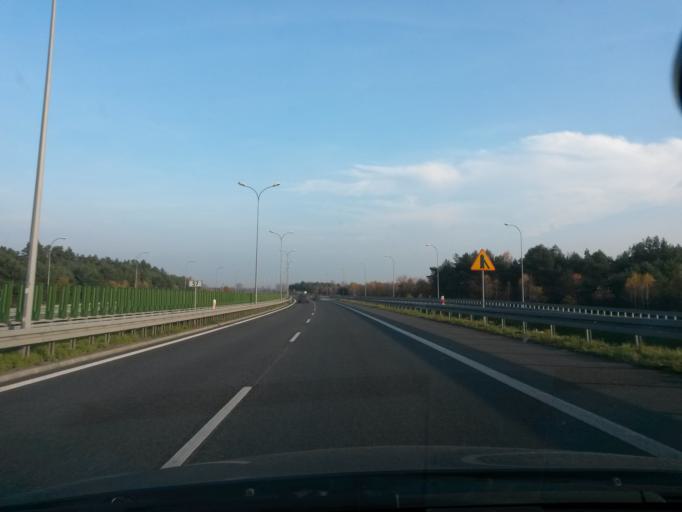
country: PL
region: Lower Silesian Voivodeship
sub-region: Powiat olesnicki
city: Olesnica
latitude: 51.2266
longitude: 17.4422
